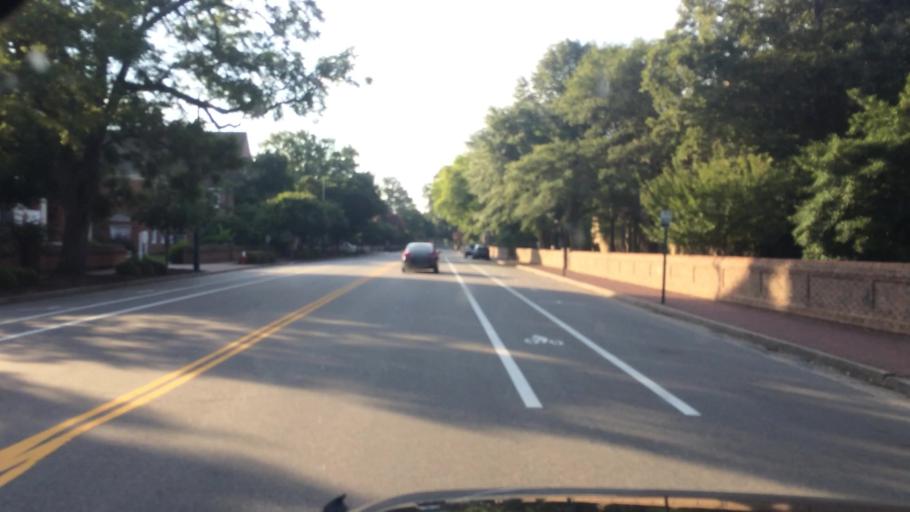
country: US
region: Virginia
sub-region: City of Williamsburg
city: Williamsburg
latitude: 37.2728
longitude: -76.7111
